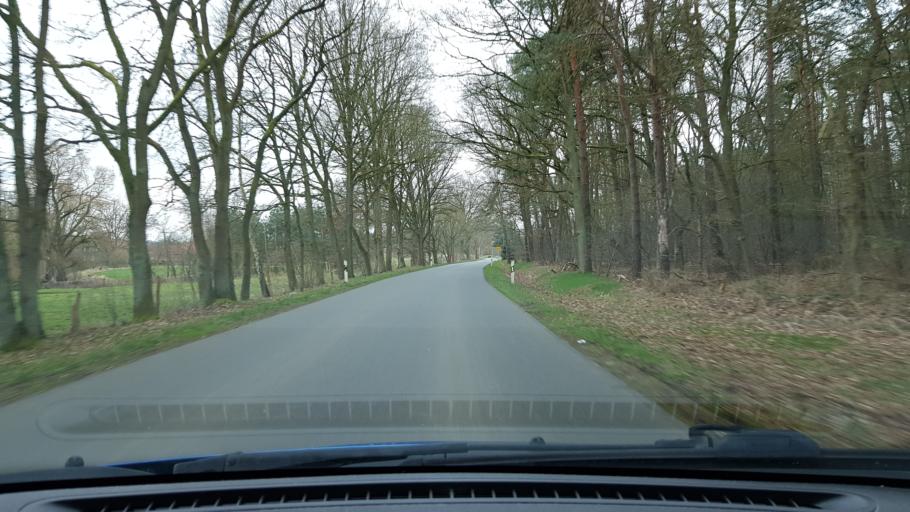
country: DE
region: Lower Saxony
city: Bad Bevensen
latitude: 53.0495
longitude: 10.6015
